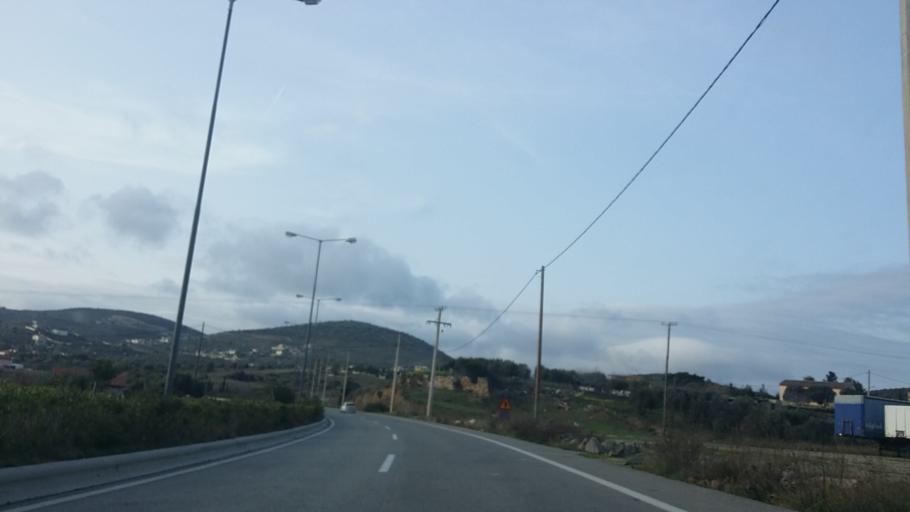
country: GR
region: Attica
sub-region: Nomarchia Anatolikis Attikis
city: Keratea
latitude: 37.8003
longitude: 24.0491
